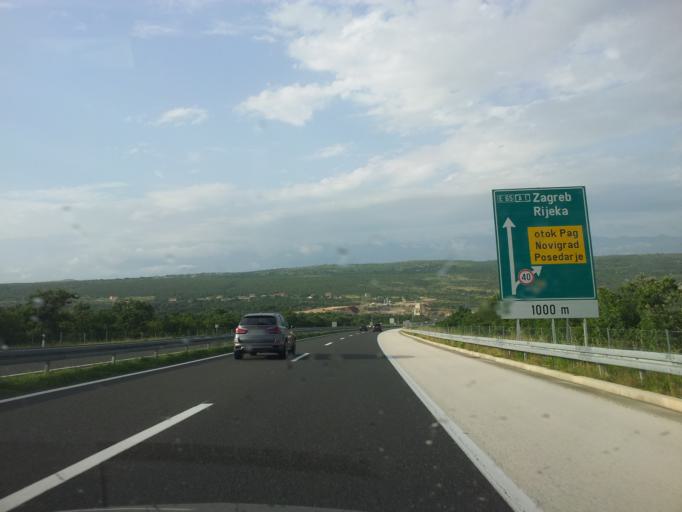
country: HR
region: Zadarska
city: Posedarje
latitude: 44.2098
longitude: 15.4463
